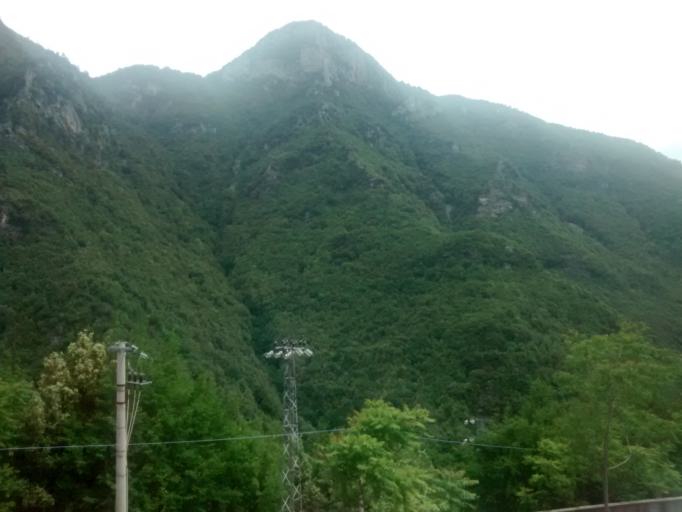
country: IT
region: Calabria
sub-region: Provincia di Cosenza
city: San Sosti
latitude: 39.6655
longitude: 16.0044
